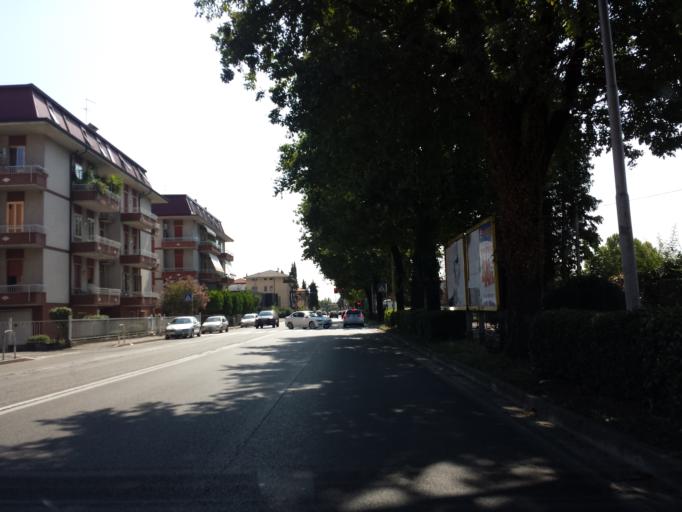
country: IT
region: Veneto
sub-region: Provincia di Vicenza
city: Vicenza
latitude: 45.5620
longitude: 11.5592
